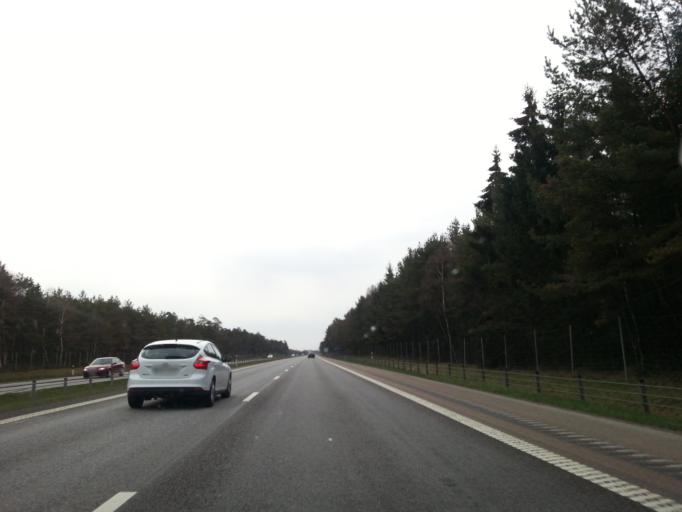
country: SE
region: Halland
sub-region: Laholms Kommun
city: Mellbystrand
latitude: 56.5528
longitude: 12.9624
